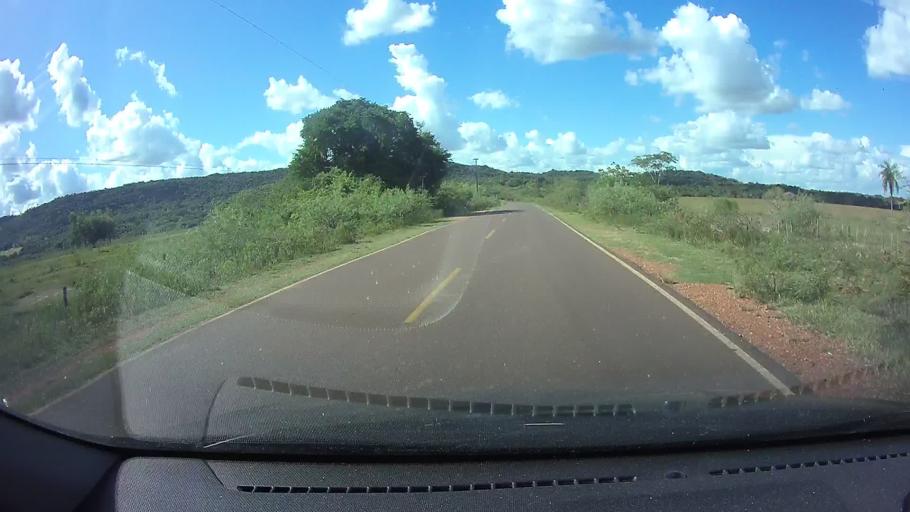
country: PY
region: Paraguari
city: Sapucai
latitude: -25.6781
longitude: -56.8623
